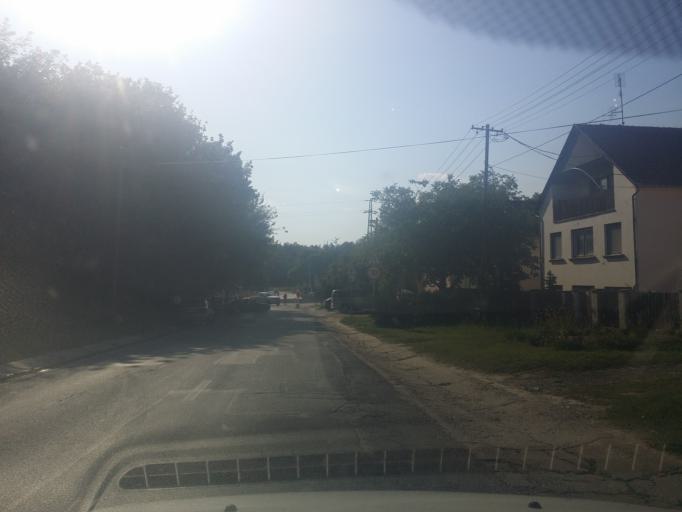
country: HU
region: Bacs-Kiskun
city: Baja
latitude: 46.1644
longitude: 18.9409
